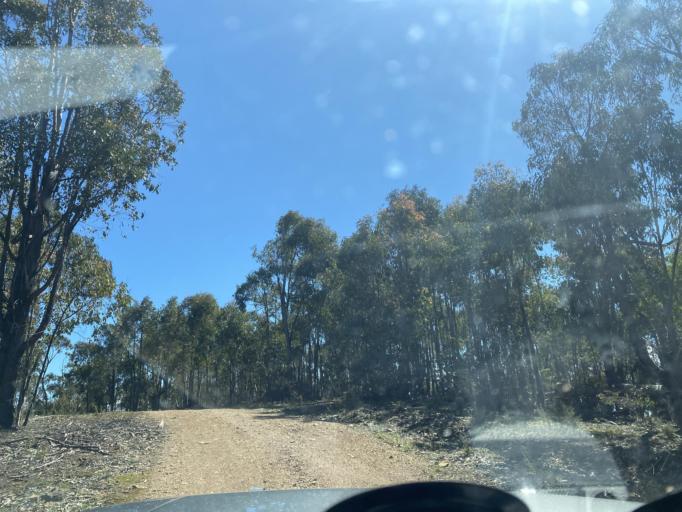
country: AU
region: Victoria
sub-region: Benalla
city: Benalla
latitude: -36.7271
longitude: 146.1827
